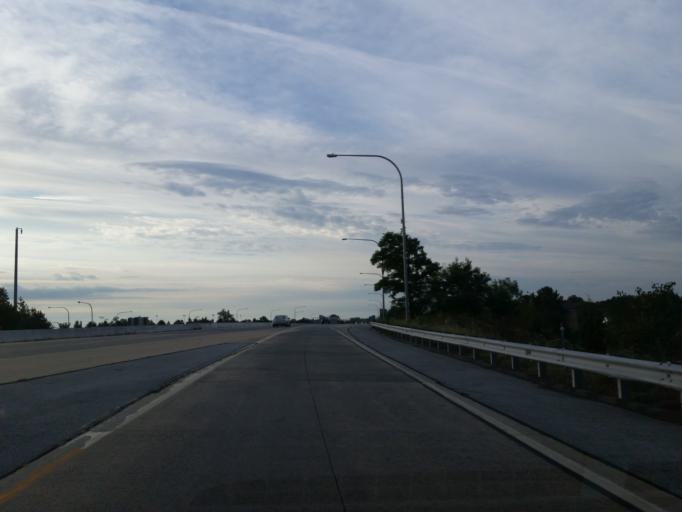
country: US
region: Delaware
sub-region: Kent County
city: Dover Base Housing
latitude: 39.1317
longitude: -75.4937
